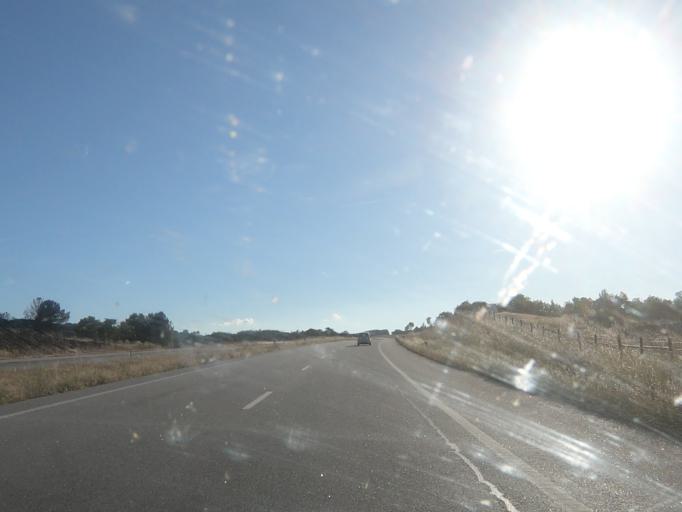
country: PT
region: Guarda
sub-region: Guarda
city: Sequeira
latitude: 40.6009
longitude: -7.1142
